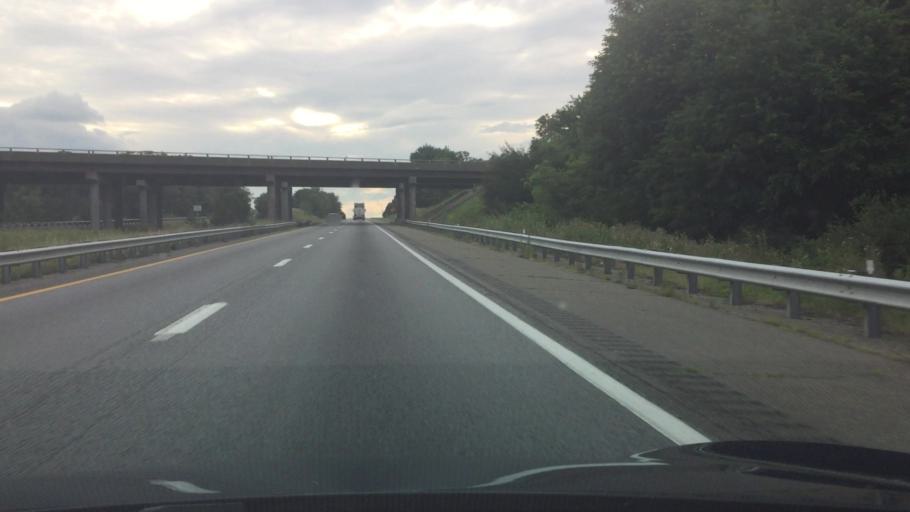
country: US
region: Virginia
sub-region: City of Radford
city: Radford
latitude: 37.0962
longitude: -80.5064
